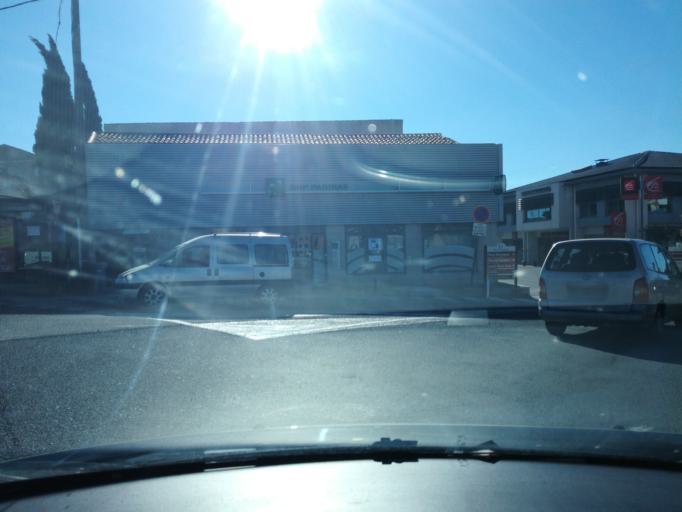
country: FR
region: Provence-Alpes-Cote d'Azur
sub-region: Departement du Var
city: Puget-sur-Argens
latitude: 43.4528
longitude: 6.6910
